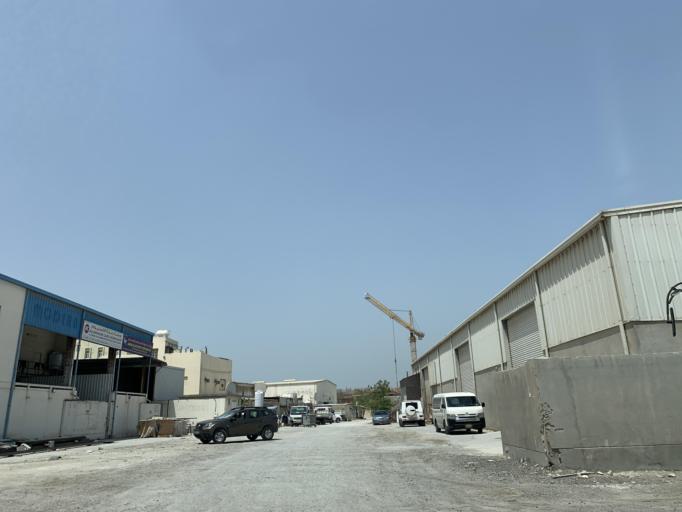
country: BH
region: Northern
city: Madinat `Isa
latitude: 26.1918
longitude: 50.5504
